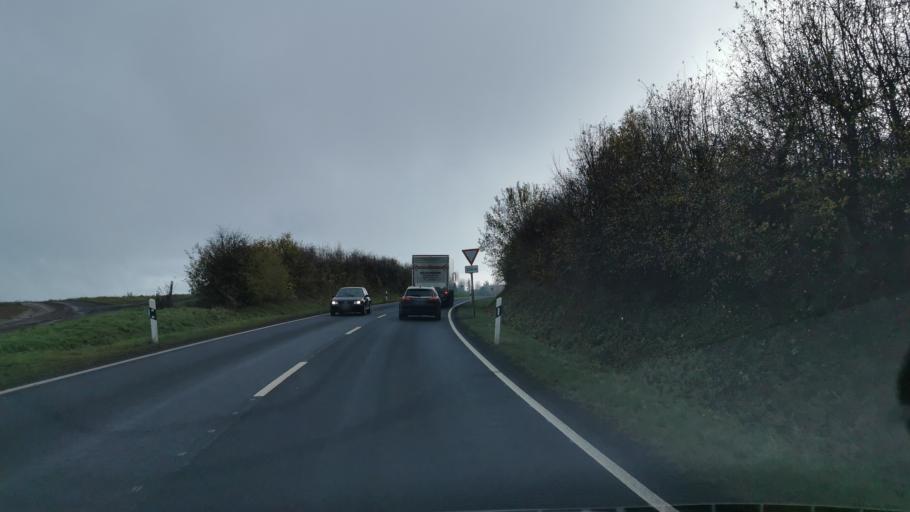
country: DE
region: Rheinland-Pfalz
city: Faid
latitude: 50.1512
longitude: 7.1164
